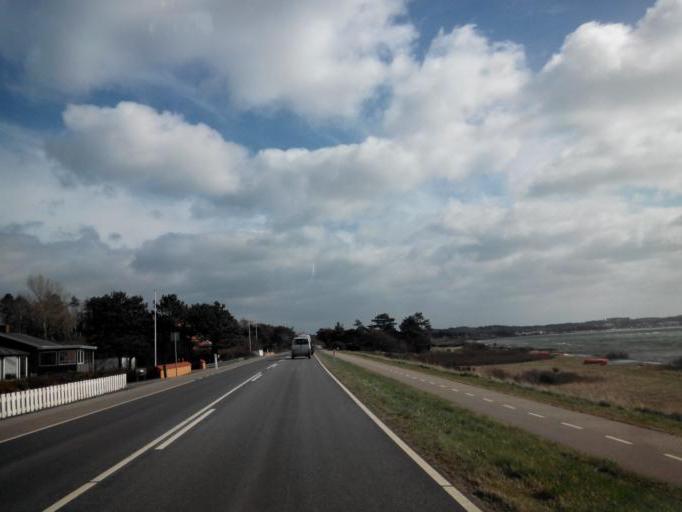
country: DK
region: Central Jutland
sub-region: Syddjurs Kommune
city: Ebeltoft
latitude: 56.2257
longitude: 10.6565
